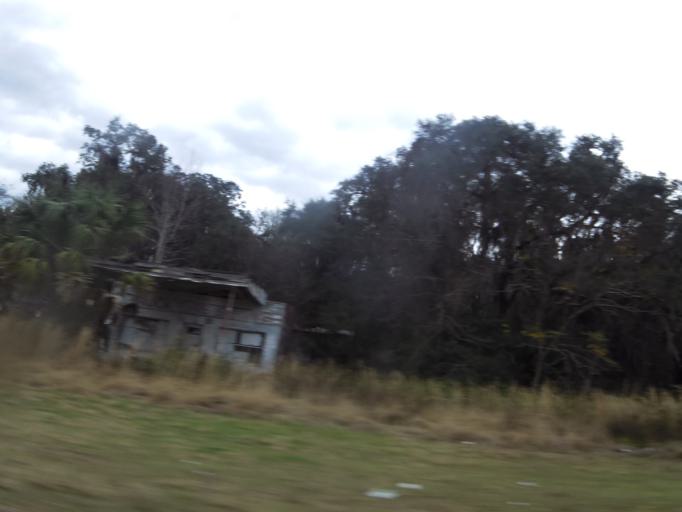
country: US
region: Florida
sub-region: Putnam County
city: Crescent City
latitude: 29.3385
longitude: -81.4985
